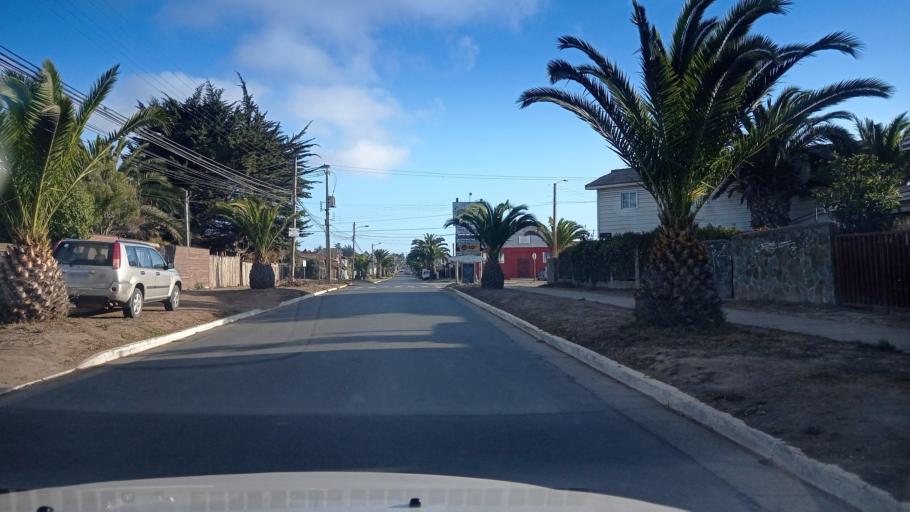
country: CL
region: O'Higgins
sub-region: Provincia de Colchagua
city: Santa Cruz
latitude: -34.3875
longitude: -72.0118
